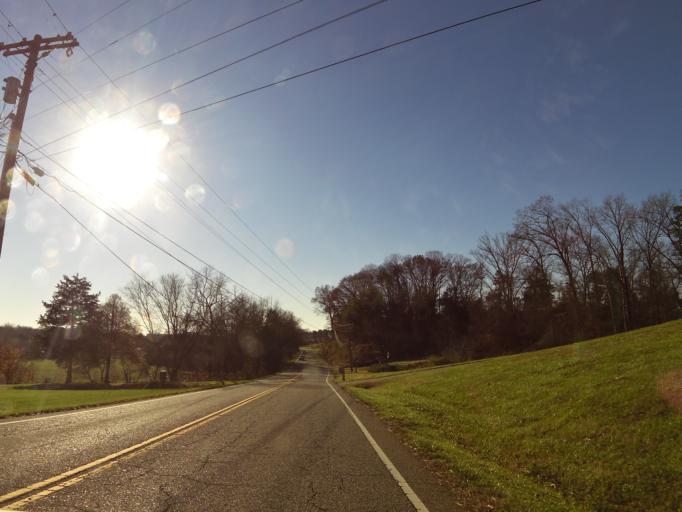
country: US
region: Tennessee
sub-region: Knox County
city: Farragut
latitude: 35.9886
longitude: -84.1117
